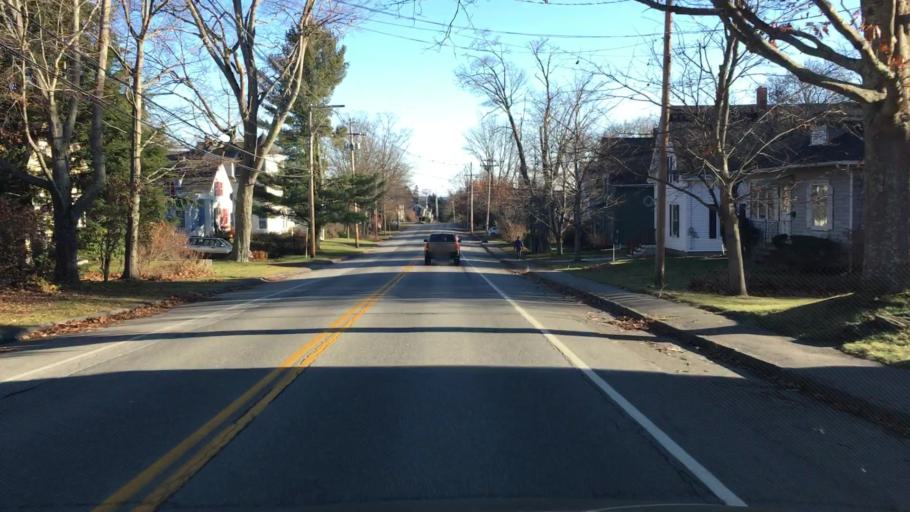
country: US
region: Maine
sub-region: Knox County
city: Camden
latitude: 44.2142
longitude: -69.0681
